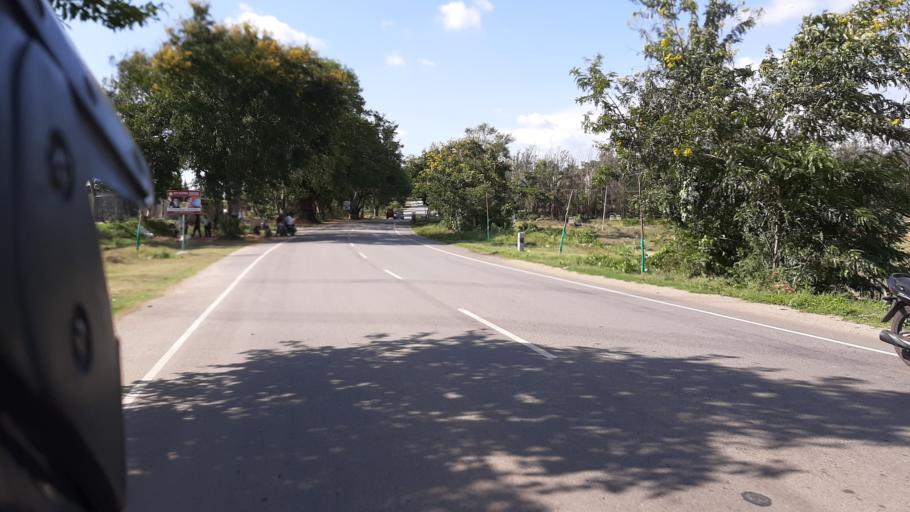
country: IN
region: Tamil Nadu
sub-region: Krishnagiri
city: Denkanikota
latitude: 12.5445
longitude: 77.7877
